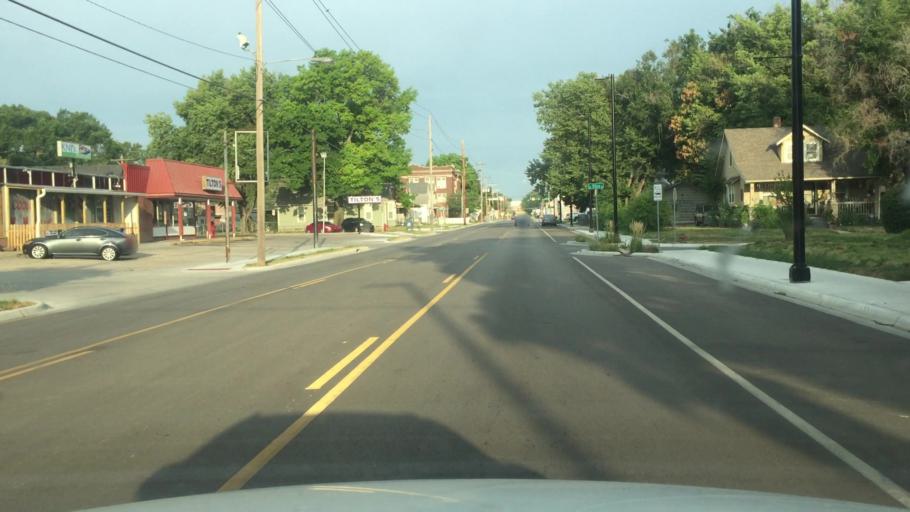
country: US
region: Kansas
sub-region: Shawnee County
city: Topeka
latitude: 39.0589
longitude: -95.6448
